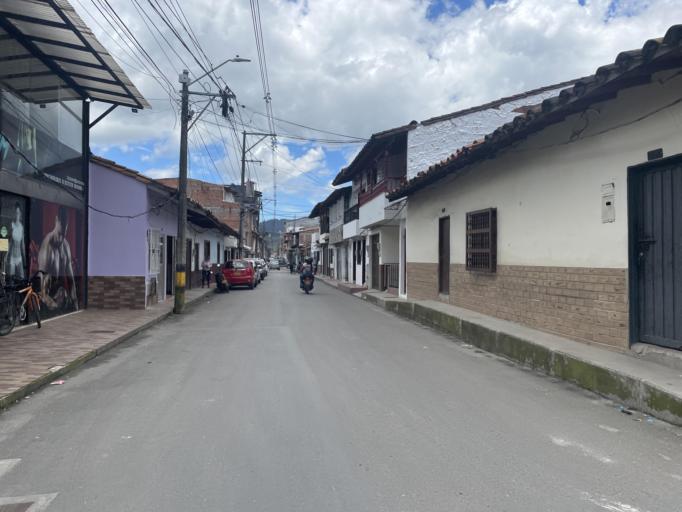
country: CO
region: Antioquia
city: La Ceja
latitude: 6.0332
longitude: -75.4296
